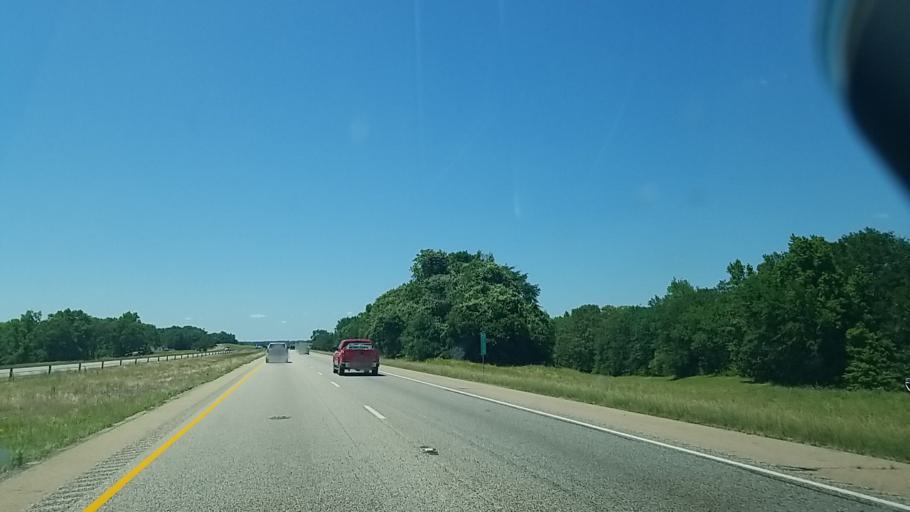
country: US
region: Texas
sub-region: Leon County
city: Buffalo
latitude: 31.3950
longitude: -96.0316
